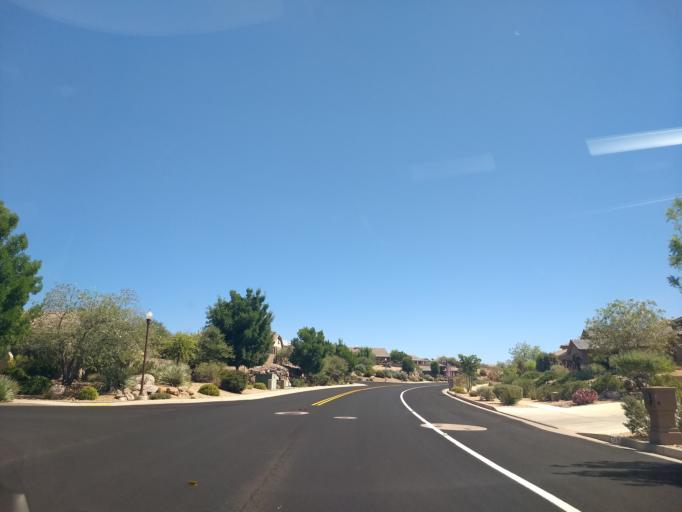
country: US
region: Utah
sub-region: Washington County
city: Washington
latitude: 37.1417
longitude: -113.4664
